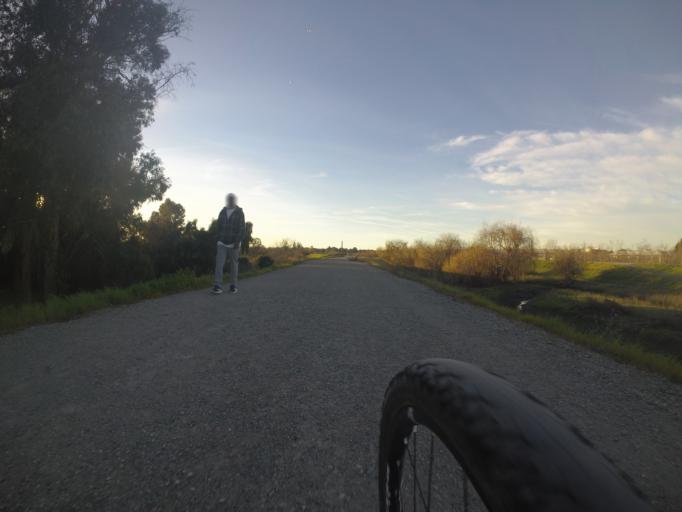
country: US
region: California
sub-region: Santa Clara County
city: Milpitas
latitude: 37.4075
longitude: -121.9556
